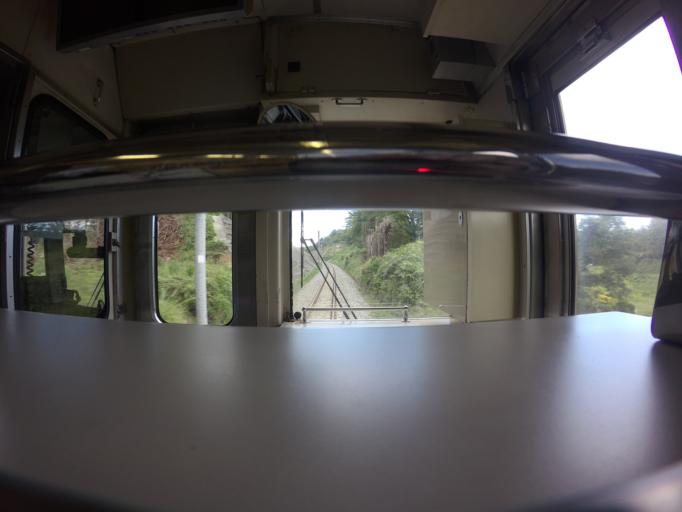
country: JP
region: Fukushima
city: Namie
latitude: 37.5452
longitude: 140.9921
